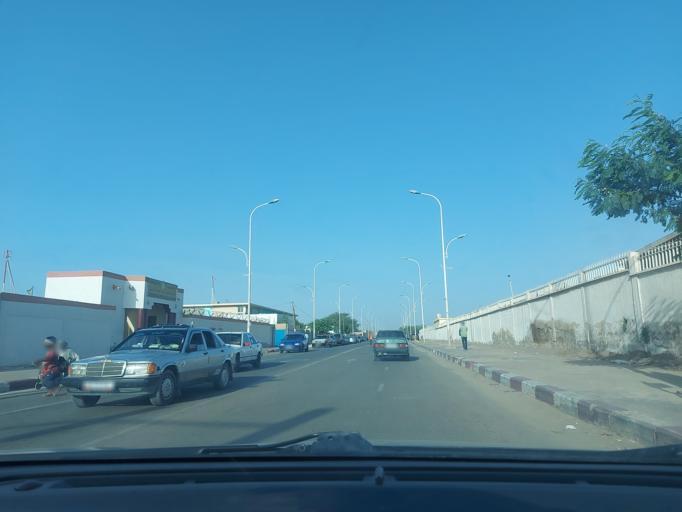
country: MR
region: Nouakchott
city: Nouakchott
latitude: 18.0867
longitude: -15.9866
